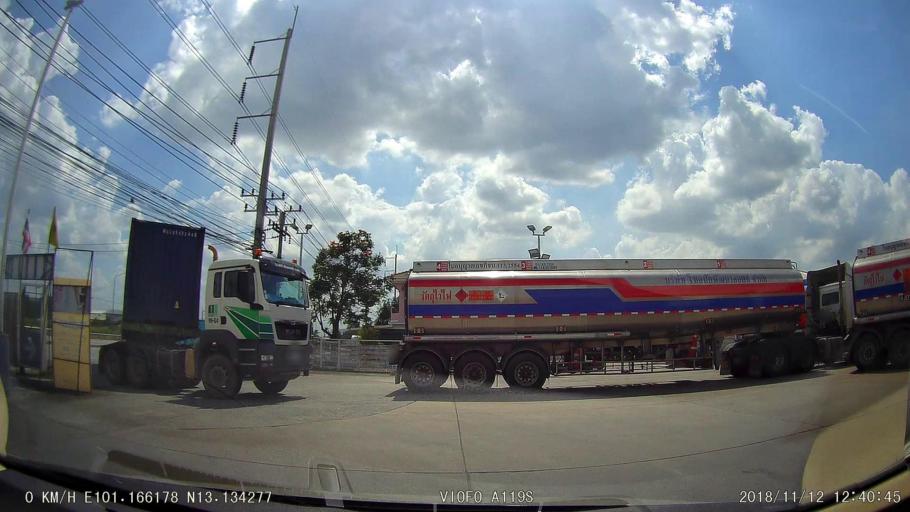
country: TH
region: Rayong
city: Pluak Daeng
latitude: 13.1361
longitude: 101.1668
